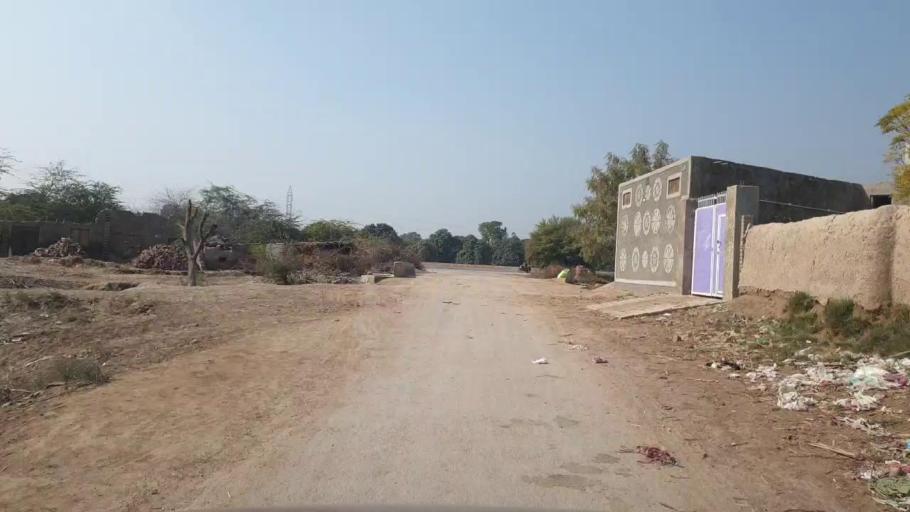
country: PK
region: Sindh
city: Bhit Shah
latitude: 25.7628
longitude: 68.4939
